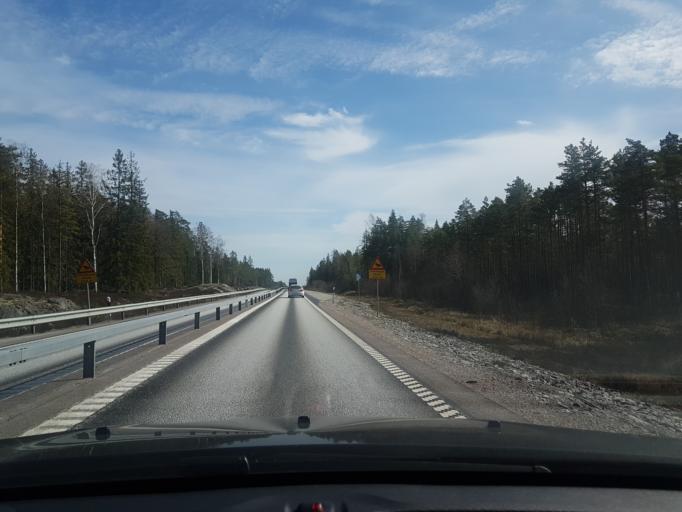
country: SE
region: Vaestmanland
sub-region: Sala Kommun
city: Sala
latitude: 59.9949
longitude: 16.4357
